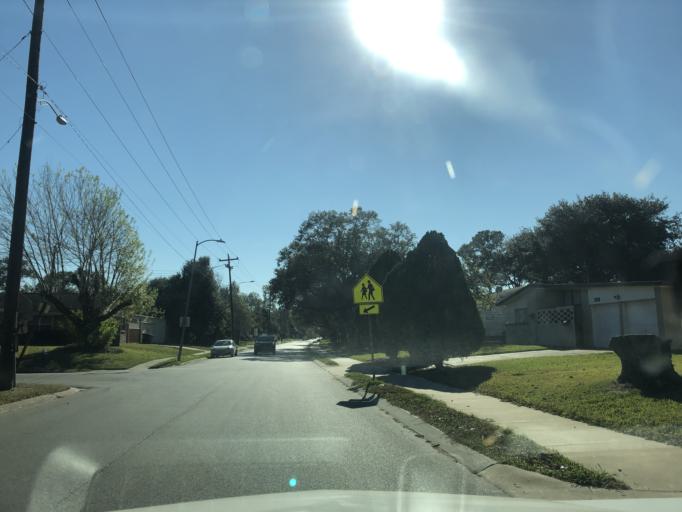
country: US
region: Texas
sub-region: Harris County
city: Bellaire
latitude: 29.6975
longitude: -95.5039
